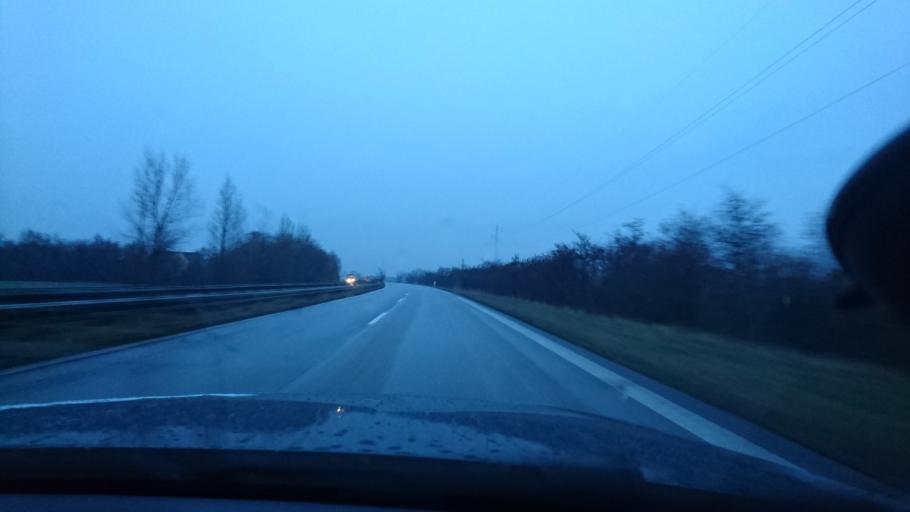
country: DK
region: Zealand
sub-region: Lolland Kommune
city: Rodby
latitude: 54.6785
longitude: 11.3947
